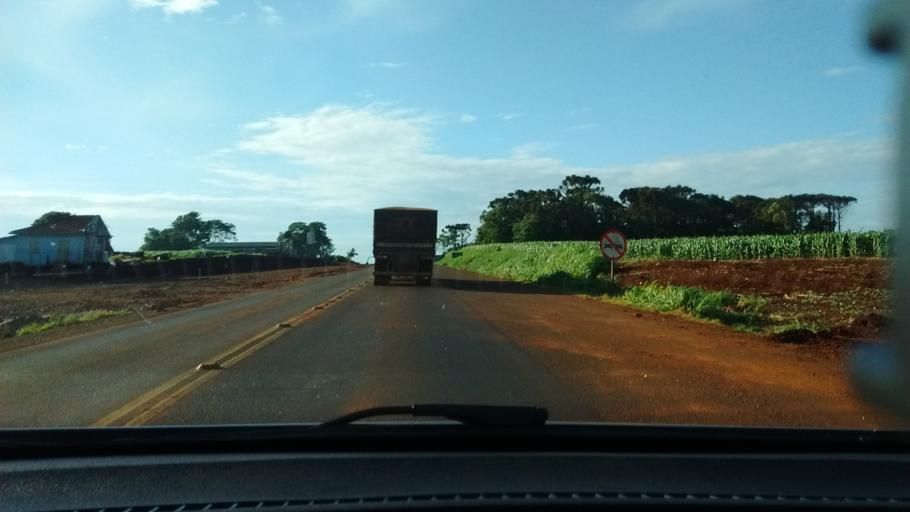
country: BR
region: Parana
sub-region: Cascavel
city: Cascavel
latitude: -25.1772
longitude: -53.6028
